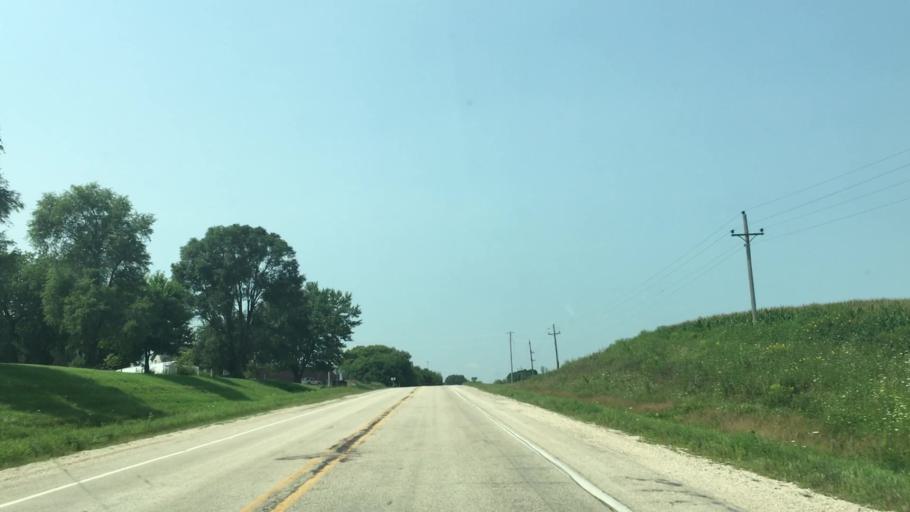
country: US
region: Iowa
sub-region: Fayette County
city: West Union
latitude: 43.0808
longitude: -91.8428
